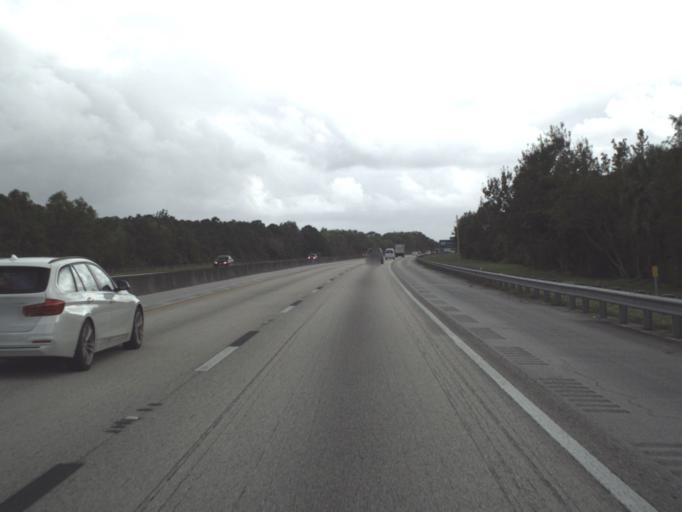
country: US
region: Florida
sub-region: Palm Beach County
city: Palm Beach Gardens
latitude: 26.8776
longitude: -80.1295
